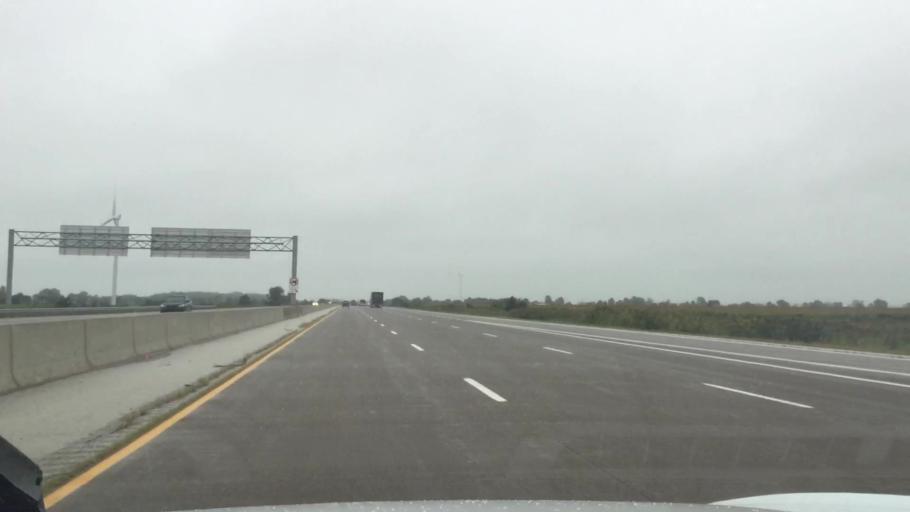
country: US
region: Michigan
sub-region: Wayne County
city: Grosse Pointe Farms
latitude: 42.2367
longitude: -82.7079
